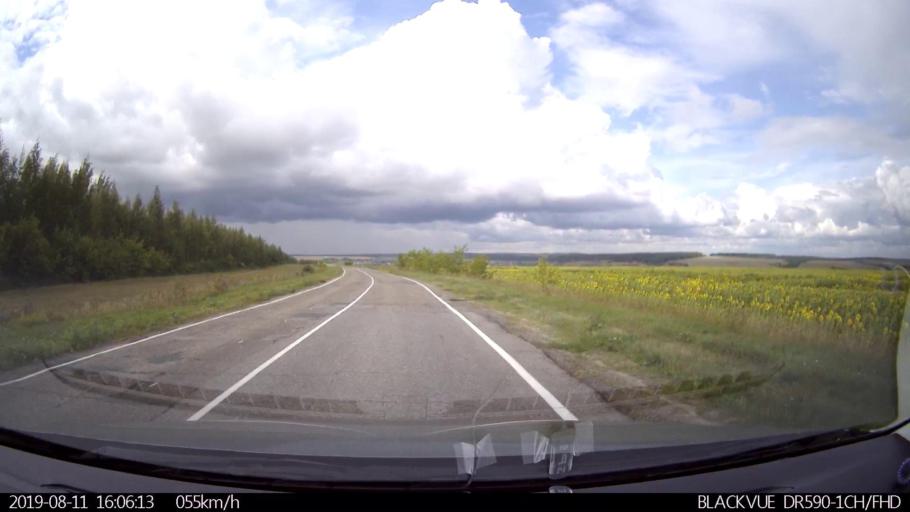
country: RU
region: Ulyanovsk
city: Ignatovka
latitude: 53.9669
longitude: 47.6492
